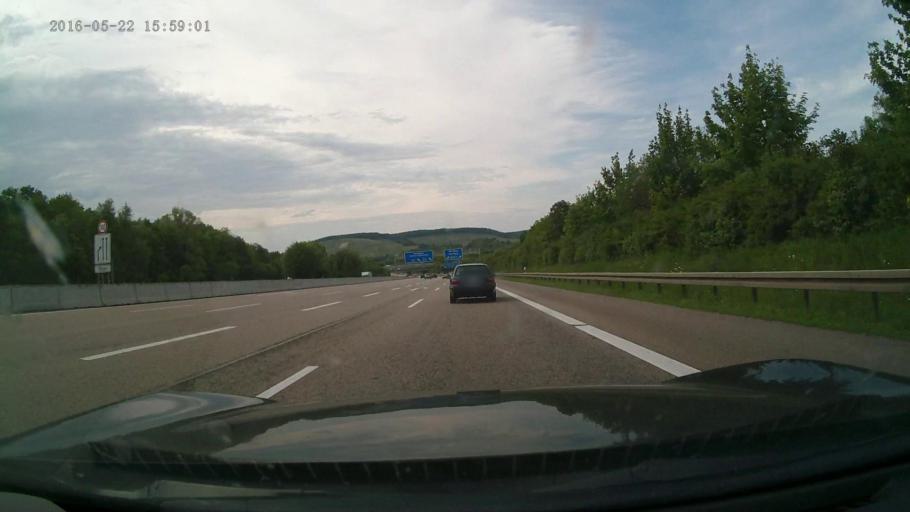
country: DE
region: Baden-Wuerttemberg
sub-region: Regierungsbezirk Stuttgart
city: Weinsberg
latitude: 49.1499
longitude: 9.3027
